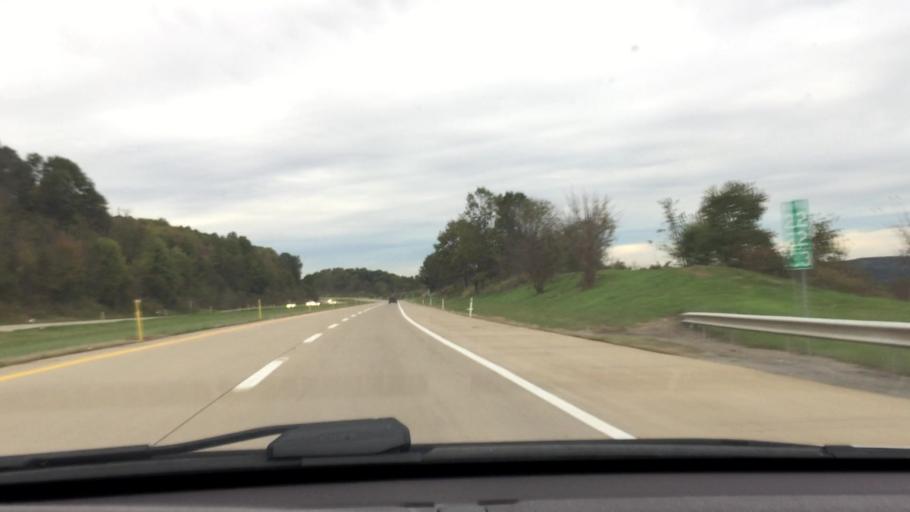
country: US
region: Pennsylvania
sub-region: Lawrence County
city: New Beaver
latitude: 40.8863
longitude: -80.3723
